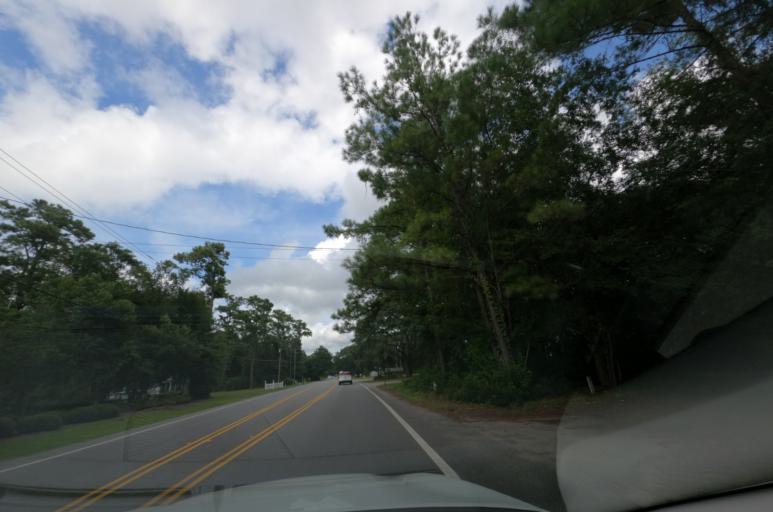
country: US
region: South Carolina
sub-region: Charleston County
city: Shell Point
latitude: 32.7316
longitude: -80.0610
